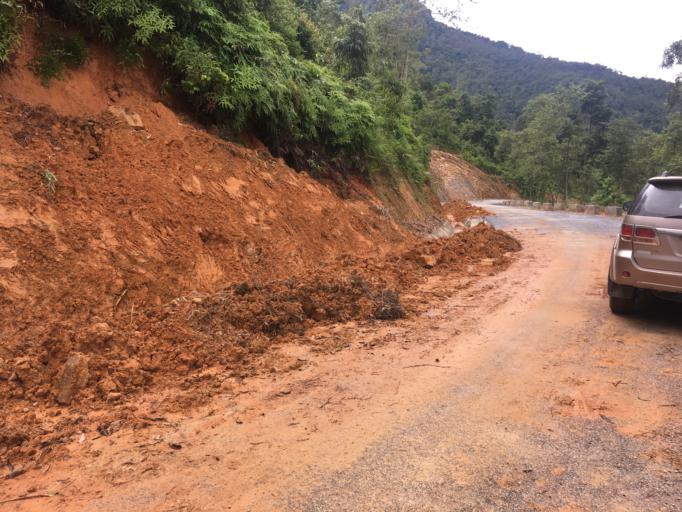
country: VN
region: Ha Giang
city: Thi Tran Tam Son
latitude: 22.9933
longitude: 105.0673
